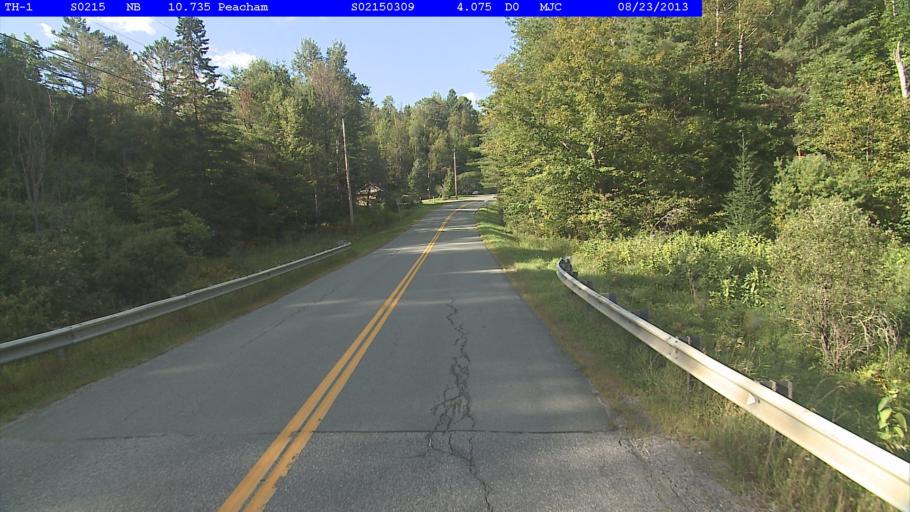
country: US
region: Vermont
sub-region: Caledonia County
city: Saint Johnsbury
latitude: 44.3550
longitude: -72.1766
